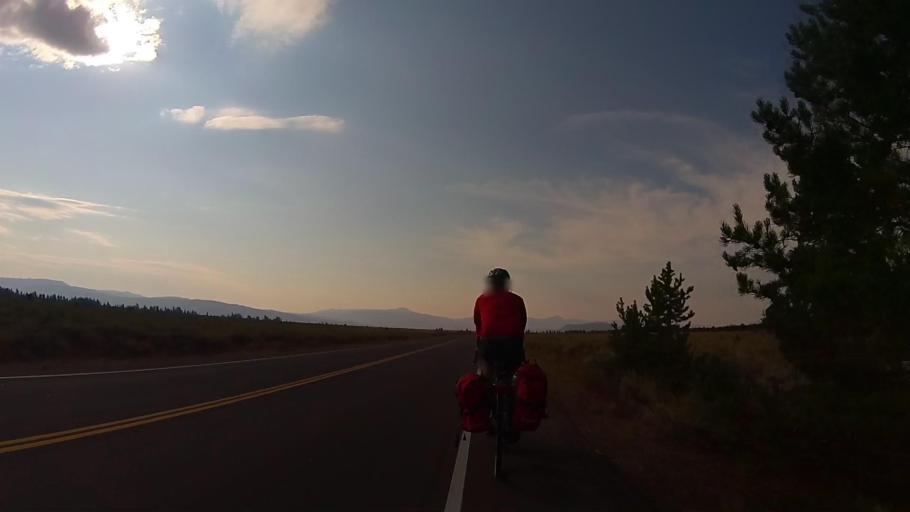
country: US
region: Wyoming
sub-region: Teton County
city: Moose Wilson Road
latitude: 43.7779
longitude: -110.7111
